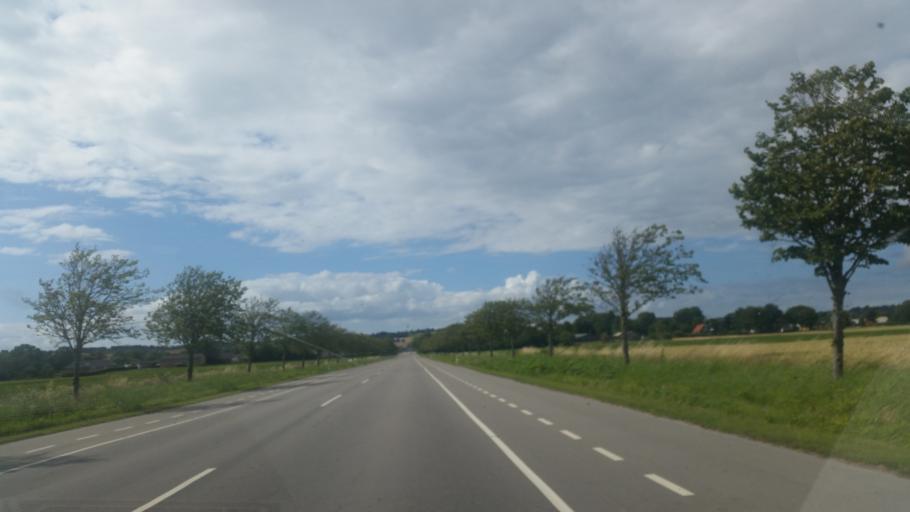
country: DK
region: Zealand
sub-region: Odsherred Kommune
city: Horve
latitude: 55.7969
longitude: 11.4504
